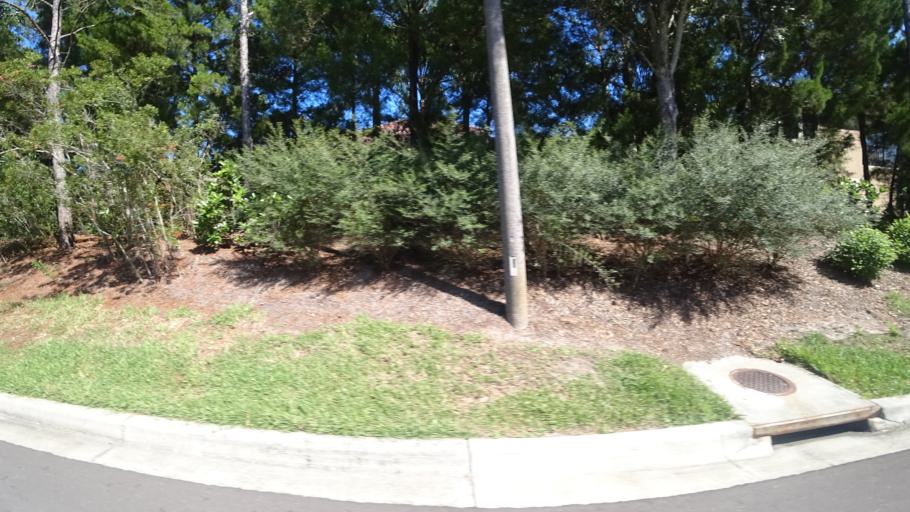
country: US
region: Florida
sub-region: Sarasota County
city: The Meadows
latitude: 27.4095
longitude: -82.4045
